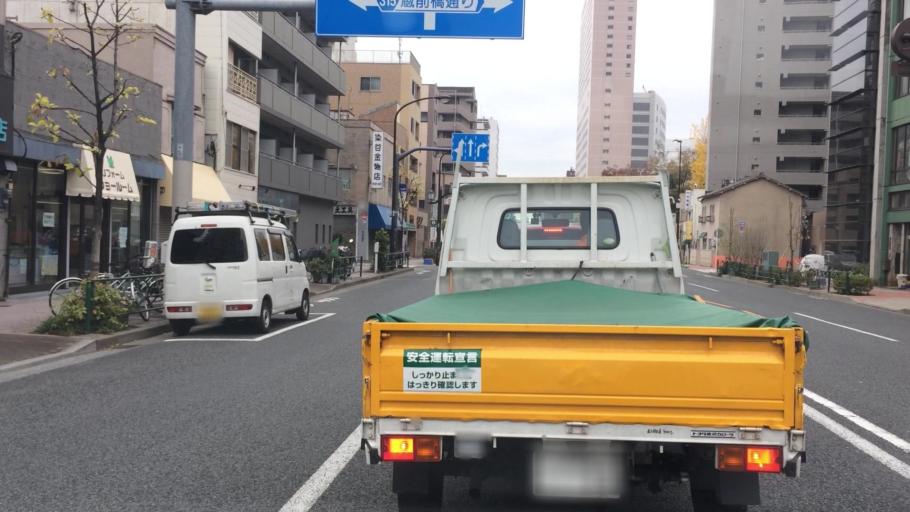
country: JP
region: Tokyo
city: Urayasu
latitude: 35.7012
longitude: 139.7970
